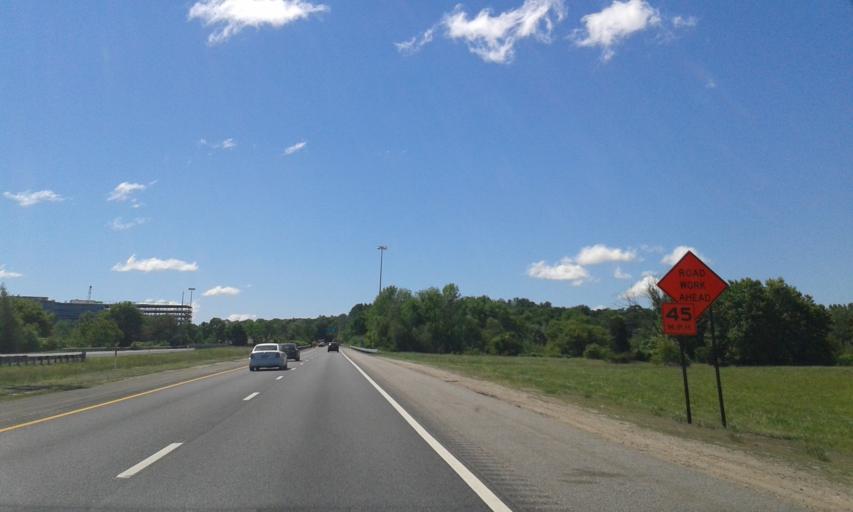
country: US
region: Massachusetts
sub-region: Middlesex County
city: Lexington
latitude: 42.4794
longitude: -71.2221
